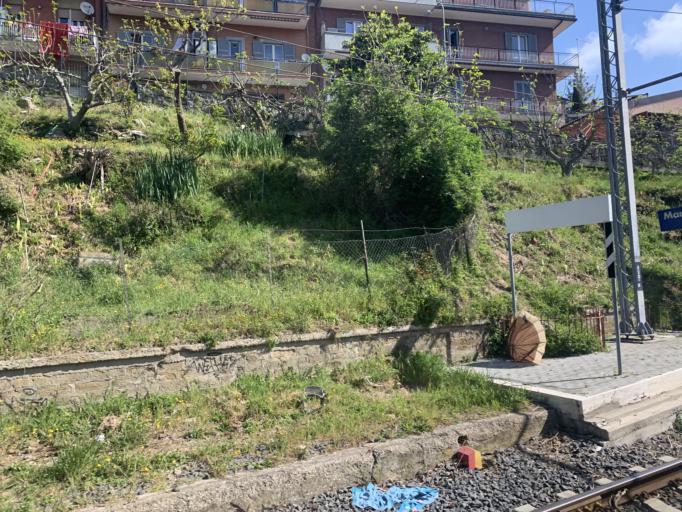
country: IT
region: Latium
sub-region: Citta metropolitana di Roma Capitale
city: Castel Gandolfo
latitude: 41.7694
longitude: 12.6549
